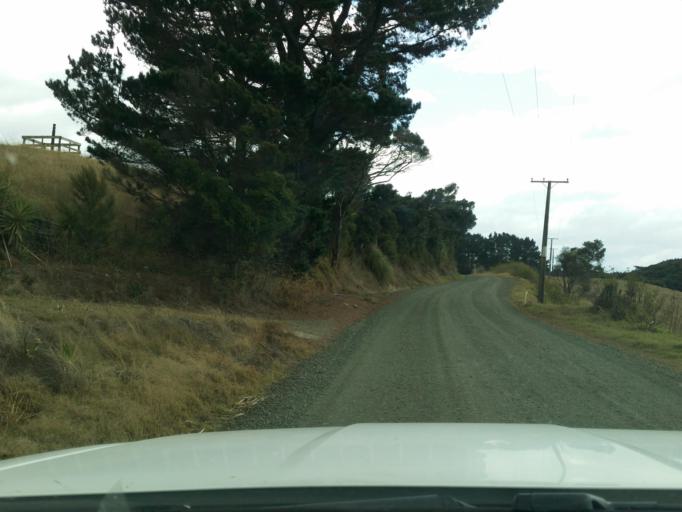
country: NZ
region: Auckland
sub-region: Auckland
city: Wellsford
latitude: -36.3220
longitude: 174.1351
